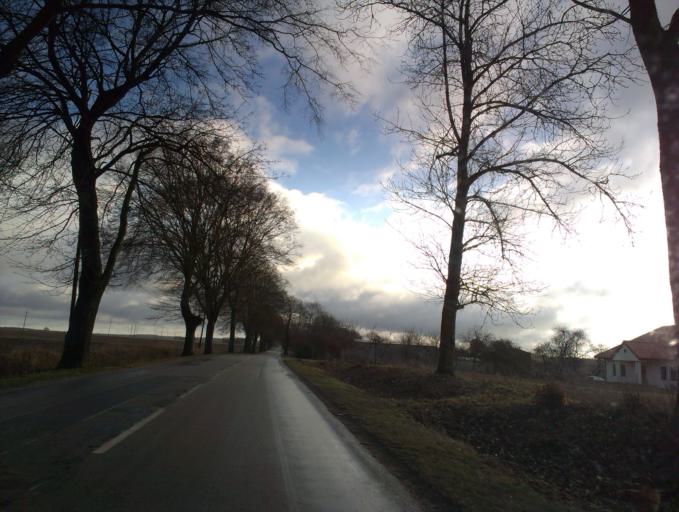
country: PL
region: Pomeranian Voivodeship
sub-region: Powiat czluchowski
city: Czarne
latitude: 53.6874
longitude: 16.9780
